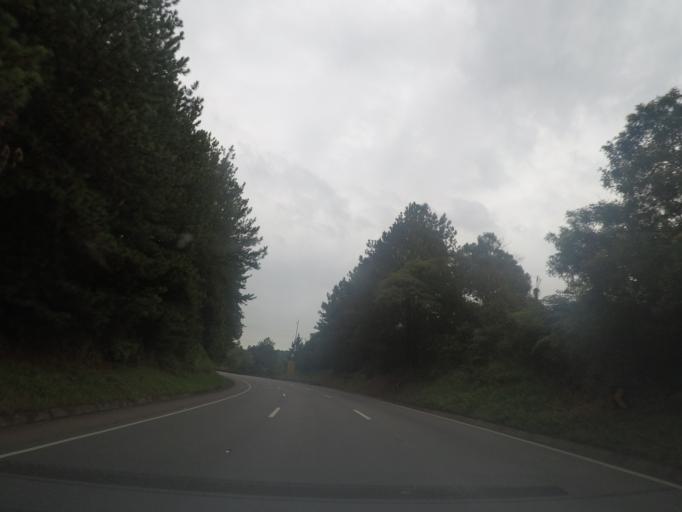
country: BR
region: Parana
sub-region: Campina Grande Do Sul
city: Campina Grande do Sul
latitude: -25.1847
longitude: -48.8862
